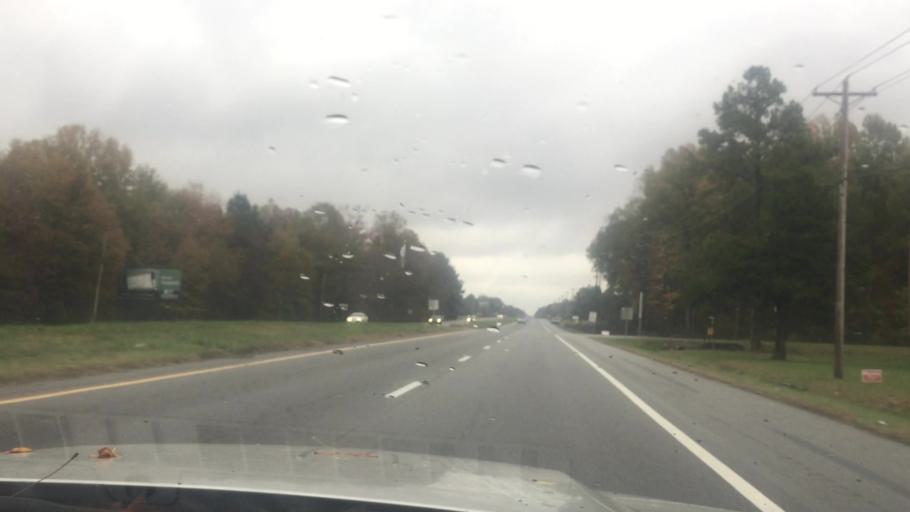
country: US
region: Tennessee
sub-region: Coffee County
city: Tullahoma
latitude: 35.3707
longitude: -86.1842
